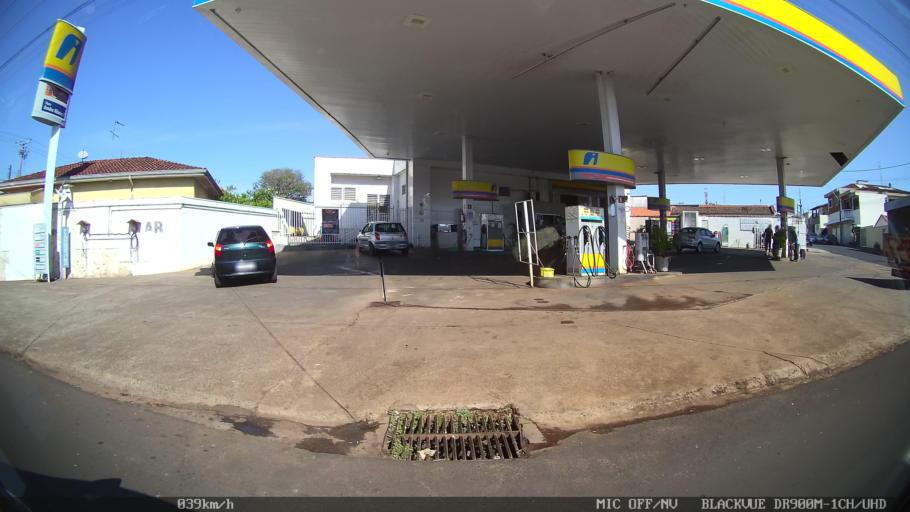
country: BR
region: Sao Paulo
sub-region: Batatais
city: Batatais
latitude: -20.8911
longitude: -47.5796
